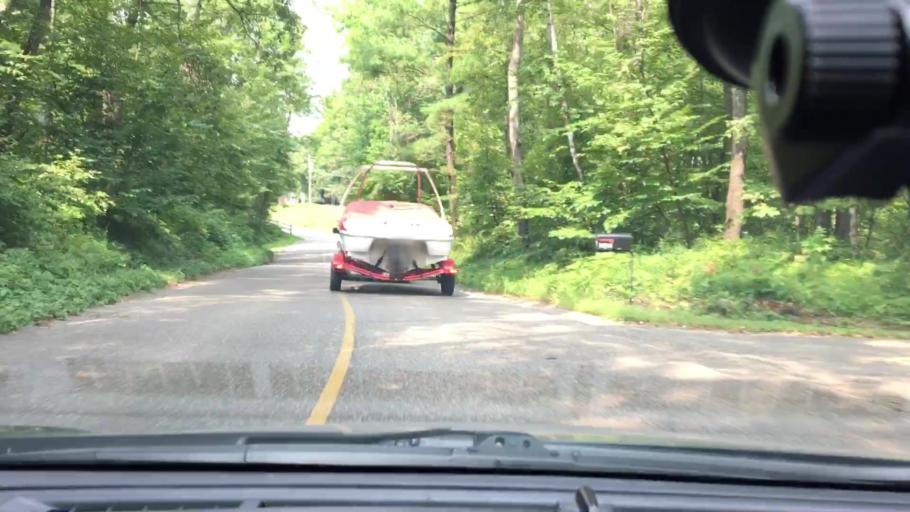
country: US
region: Minnesota
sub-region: Cass County
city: East Gull Lake
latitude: 46.4099
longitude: -94.3540
